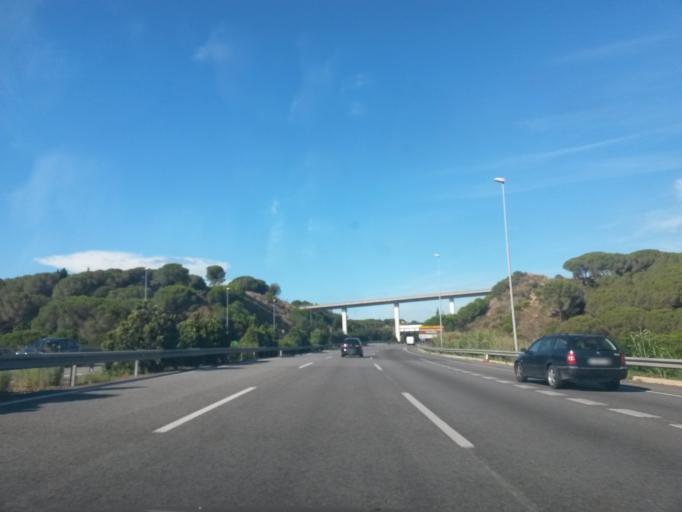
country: ES
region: Catalonia
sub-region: Provincia de Barcelona
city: Caldes d'Estrac
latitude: 41.5791
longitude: 2.5291
